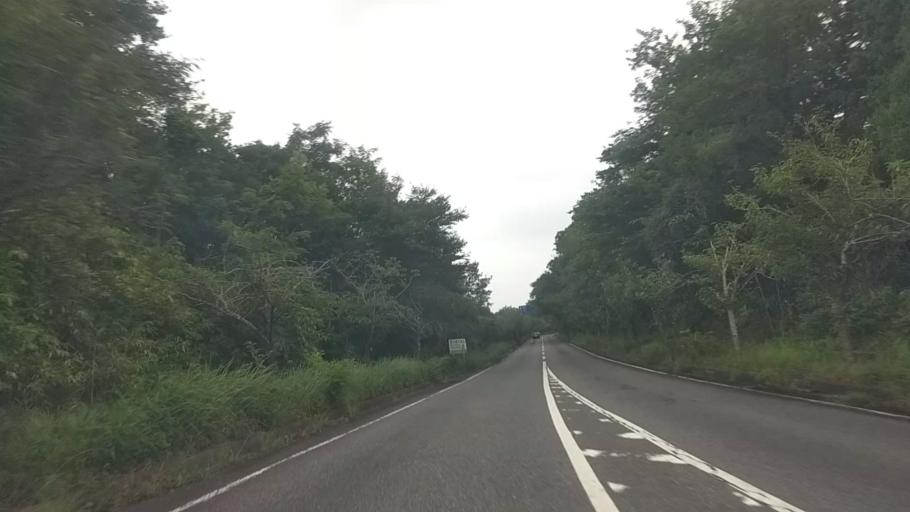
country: JP
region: Chiba
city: Kisarazu
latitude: 35.3844
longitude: 140.0059
